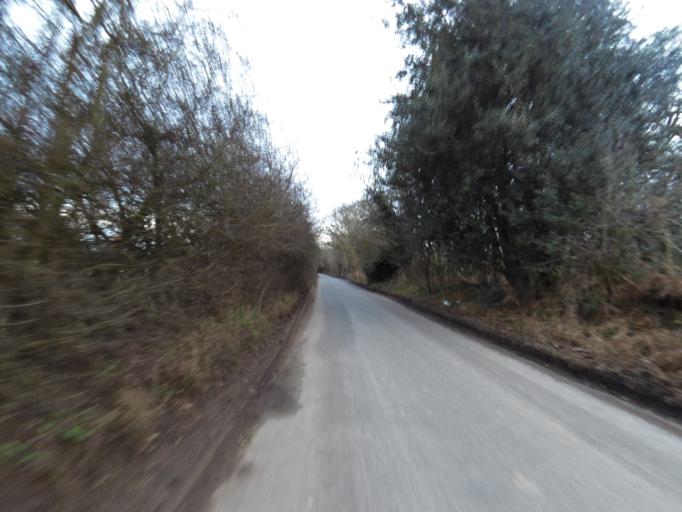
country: GB
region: England
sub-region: Suffolk
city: Ipswich
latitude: 52.0200
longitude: 1.1140
